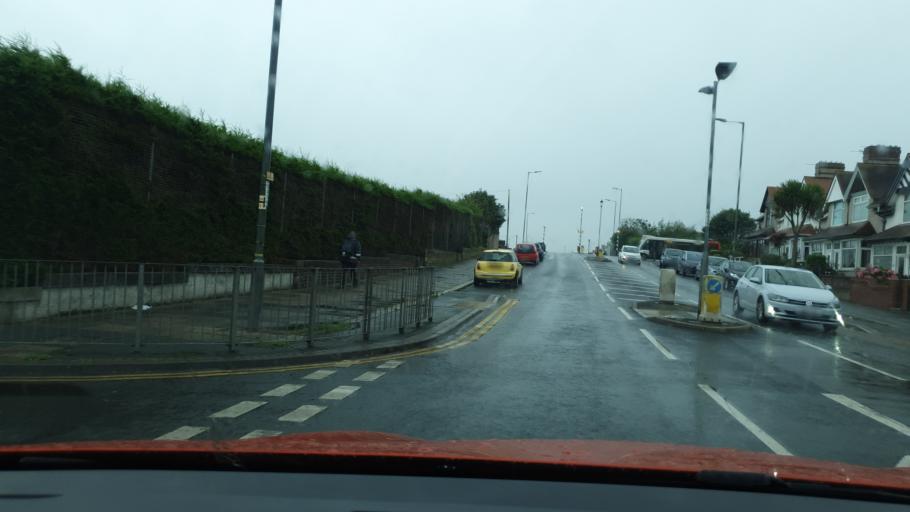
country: GB
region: England
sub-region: Cumbria
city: Barrow in Furness
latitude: 54.1031
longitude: -3.2479
